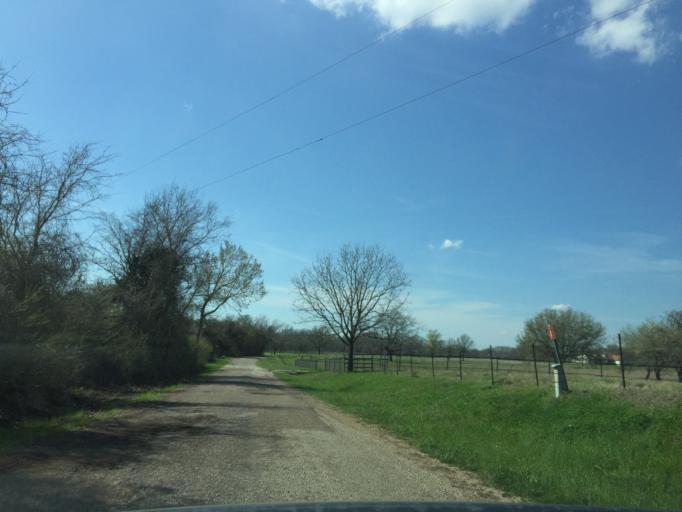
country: US
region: Texas
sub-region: Milam County
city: Thorndale
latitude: 30.5626
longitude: -97.1509
